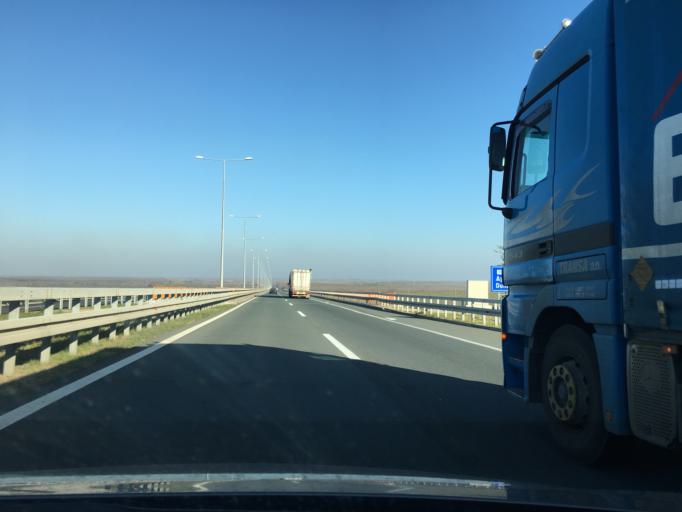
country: RS
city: Beska
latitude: 45.1647
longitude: 20.0807
